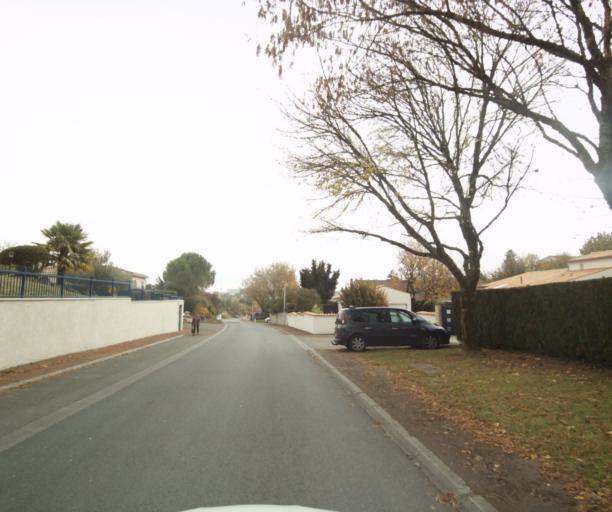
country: FR
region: Poitou-Charentes
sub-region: Departement de la Charente-Maritime
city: Saintes
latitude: 45.7435
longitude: -0.6543
